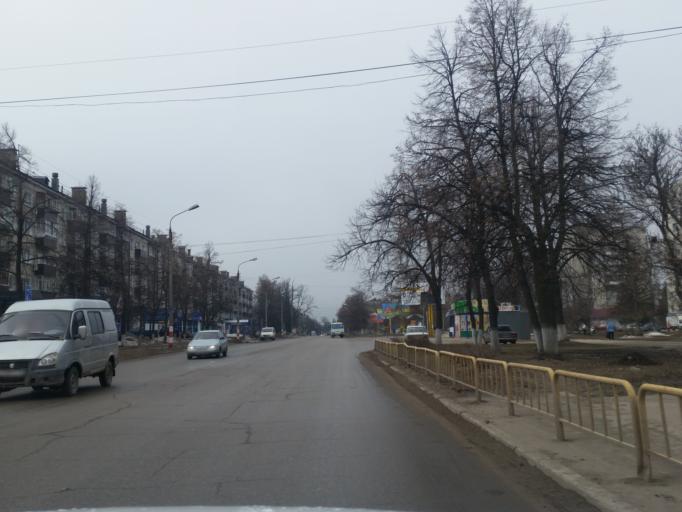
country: RU
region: Ulyanovsk
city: Dimitrovgrad
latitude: 54.2300
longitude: 49.5526
